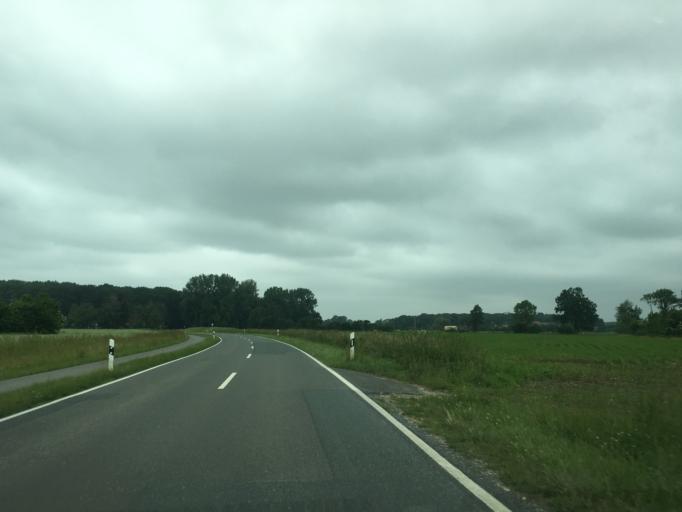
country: DE
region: North Rhine-Westphalia
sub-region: Regierungsbezirk Munster
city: Altenberge
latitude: 52.0066
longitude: 7.4903
